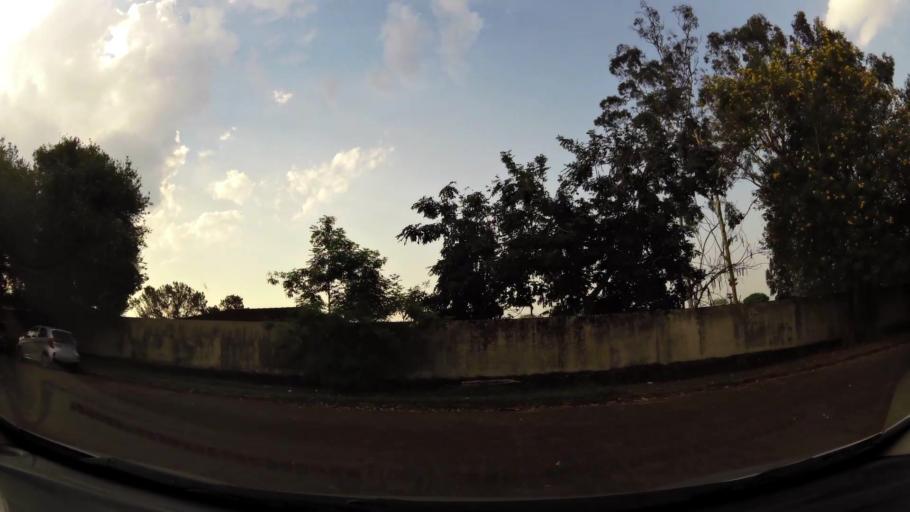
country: PY
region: Alto Parana
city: Presidente Franco
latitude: -25.5202
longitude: -54.6324
